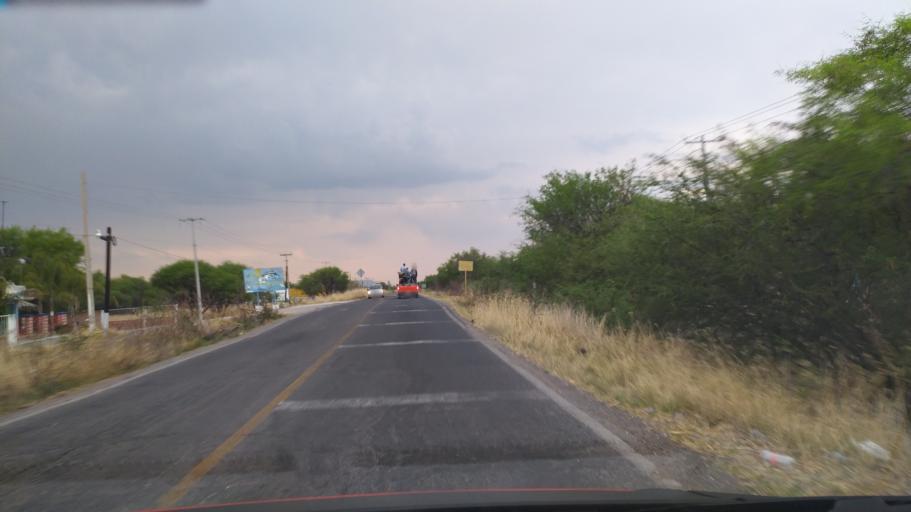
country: MX
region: Guanajuato
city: Ciudad Manuel Doblado
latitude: 20.7978
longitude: -101.9057
